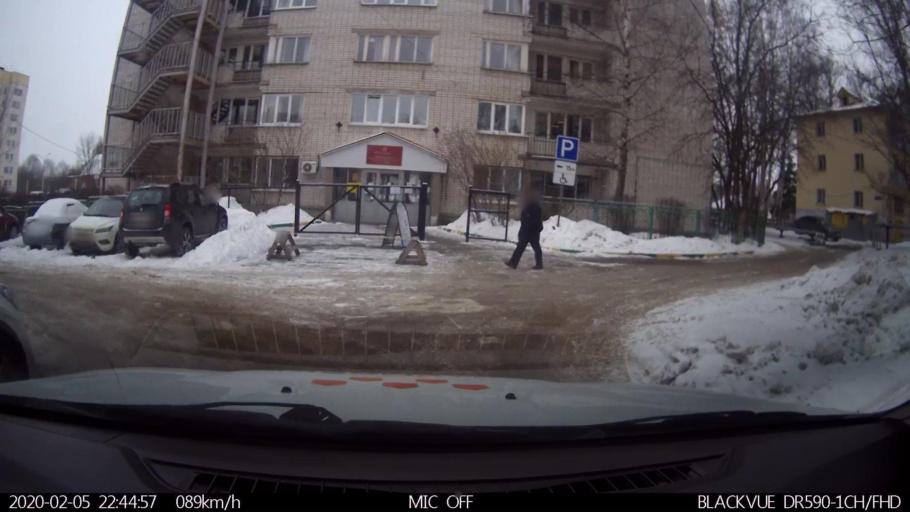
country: RU
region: Nizjnij Novgorod
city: Imeni Stepana Razina
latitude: 54.7047
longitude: 44.4120
